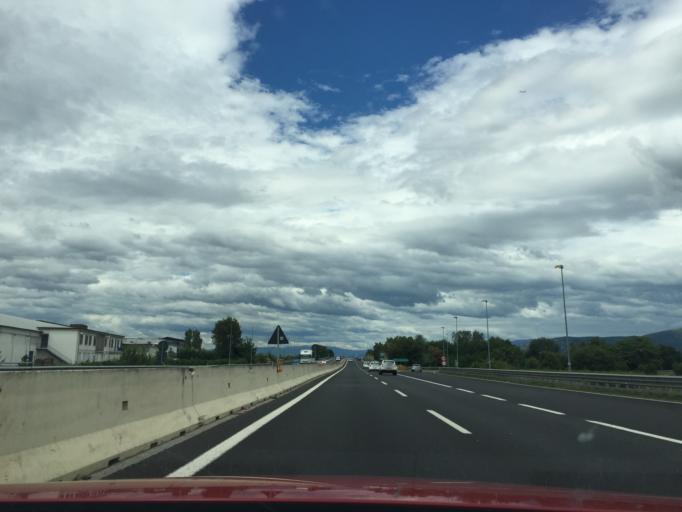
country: IT
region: Tuscany
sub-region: Province of Florence
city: Sesto Fiorentino
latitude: 43.8084
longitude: 11.1895
